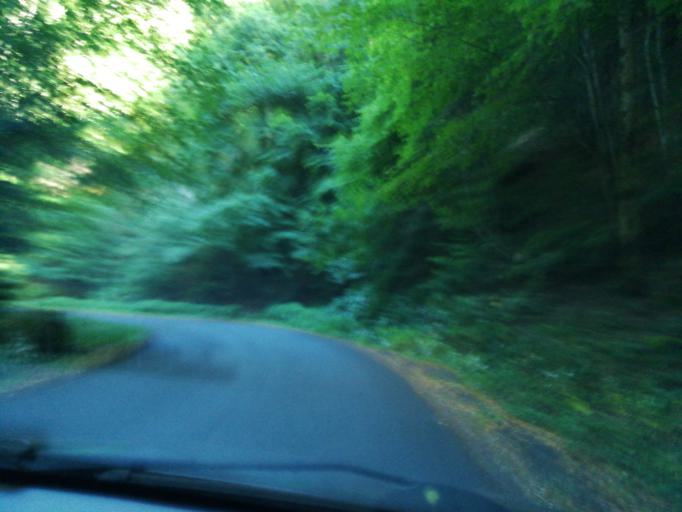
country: FR
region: Auvergne
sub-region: Departement du Cantal
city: Saint-Cernin
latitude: 45.0964
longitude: 2.5535
